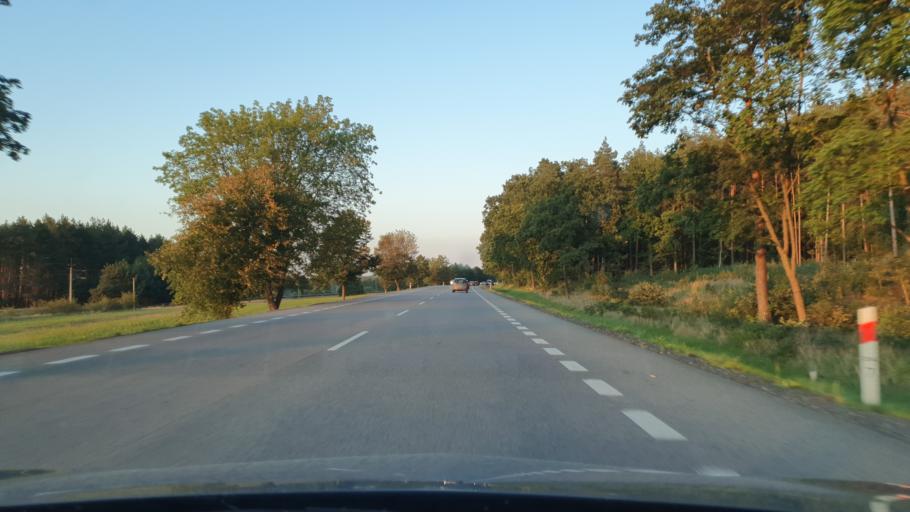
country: PL
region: Pomeranian Voivodeship
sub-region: Powiat leborski
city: Nowa Wies Leborska
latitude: 54.5215
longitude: 17.6874
